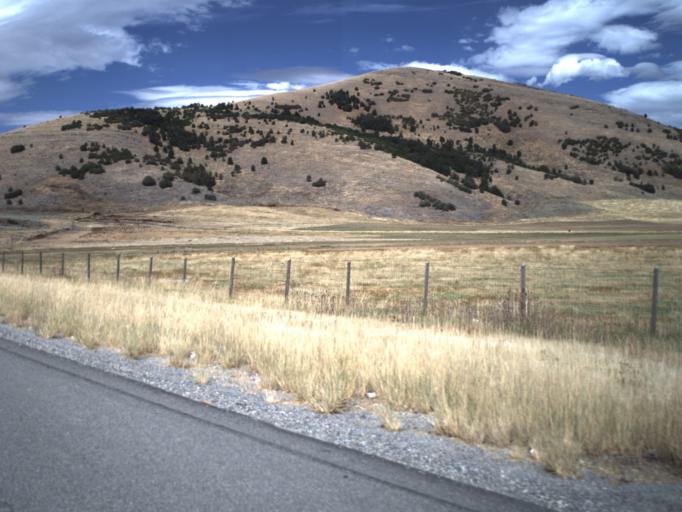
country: US
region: Utah
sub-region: Box Elder County
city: Brigham City
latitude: 41.5697
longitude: -111.9676
